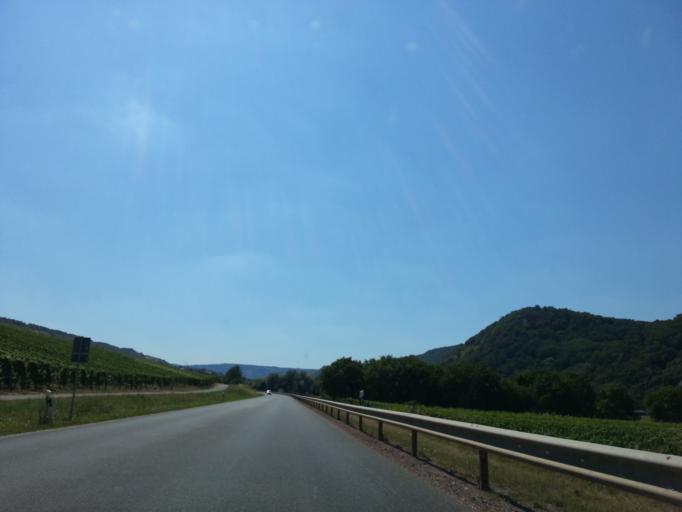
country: DE
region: Rheinland-Pfalz
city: Piesport
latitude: 49.8709
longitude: 6.8997
